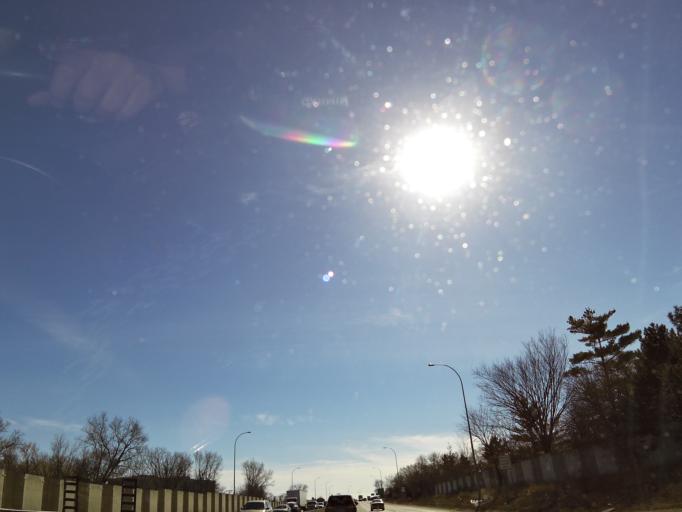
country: US
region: Minnesota
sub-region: Hennepin County
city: Minnetonka Mills
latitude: 44.9313
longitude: -93.3976
